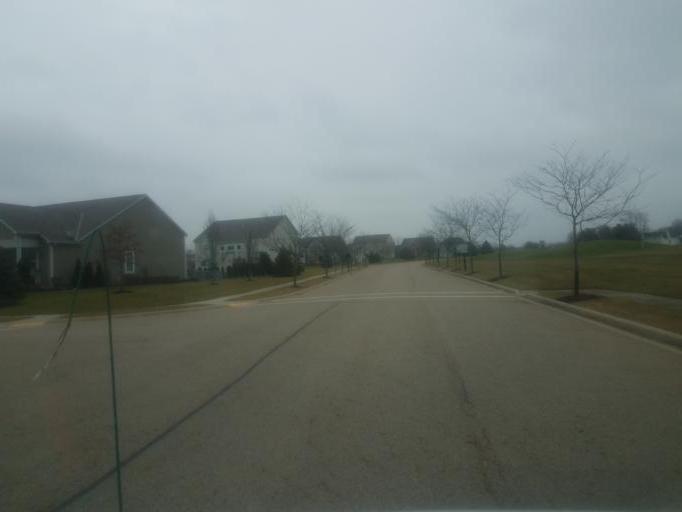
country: US
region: Ohio
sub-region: Franklin County
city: Westerville
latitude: 40.1910
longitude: -82.9308
